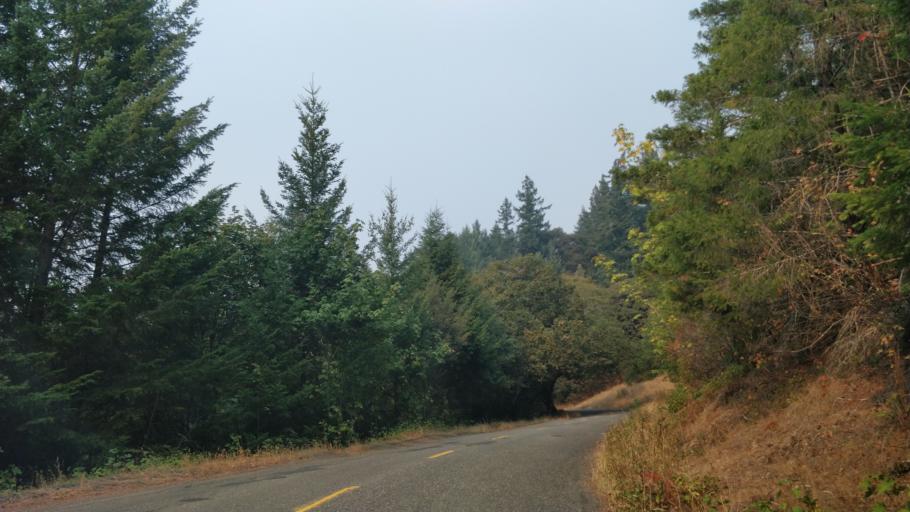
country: US
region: California
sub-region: Humboldt County
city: Rio Dell
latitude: 40.2514
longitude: -124.1252
